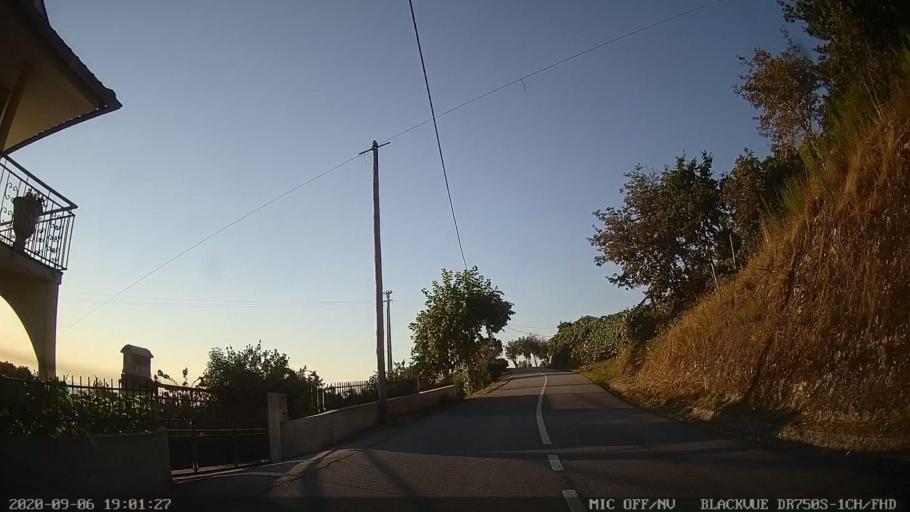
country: PT
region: Porto
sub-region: Baiao
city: Baiao
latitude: 41.2345
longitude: -7.9987
